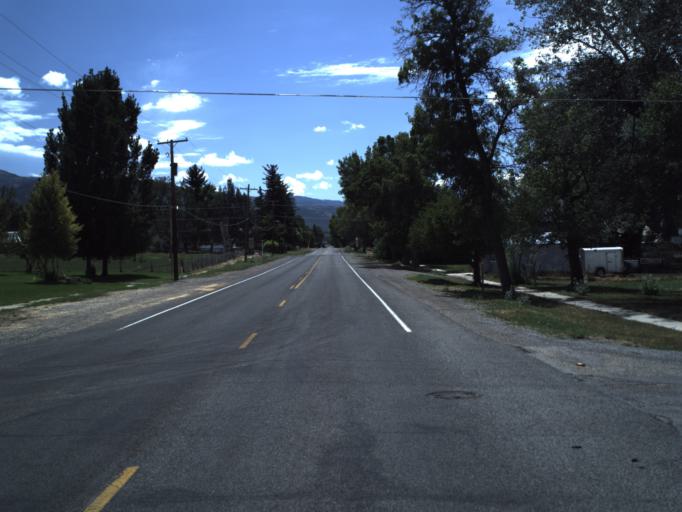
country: US
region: Utah
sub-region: Sanpete County
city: Mount Pleasant
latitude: 39.4838
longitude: -111.4961
